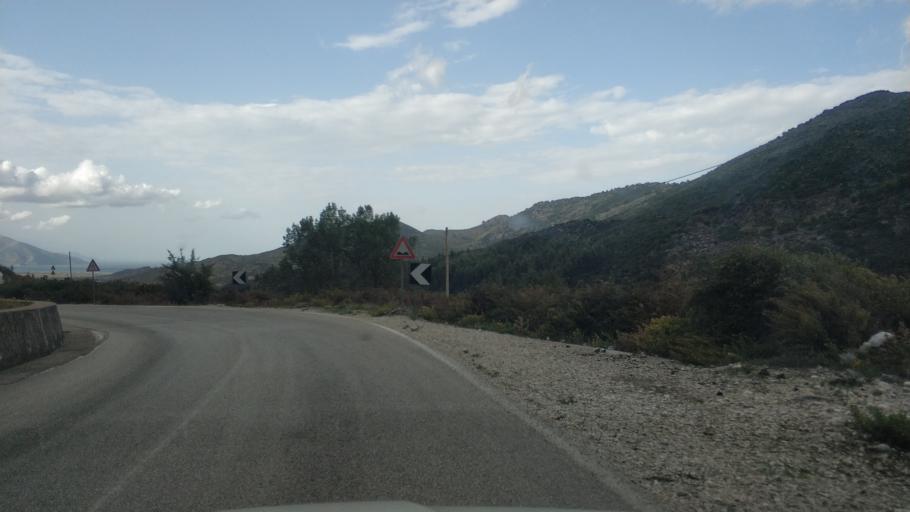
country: AL
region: Vlore
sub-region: Rrethi i Vlores
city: Orikum
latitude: 40.2611
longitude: 19.5240
